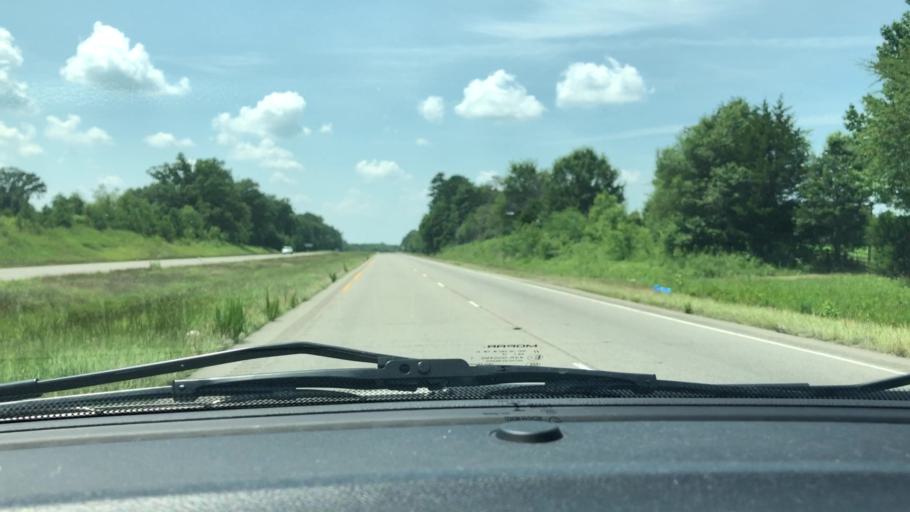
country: US
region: North Carolina
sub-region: Chatham County
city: Farmville
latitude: 35.6065
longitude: -79.3301
